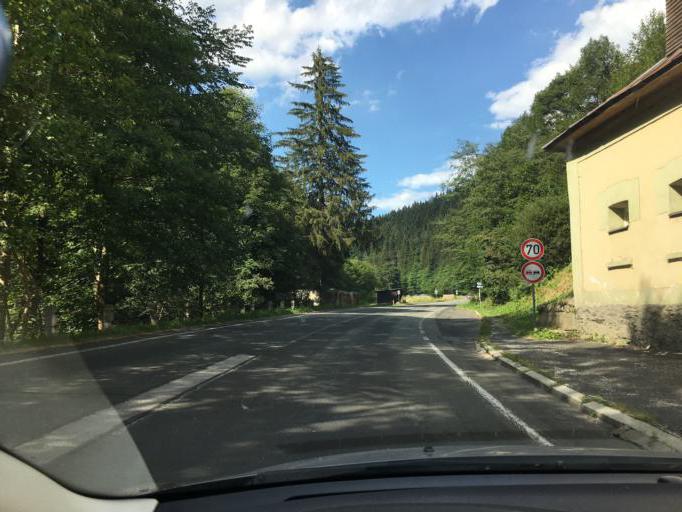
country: CZ
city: Benecko
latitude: 50.6871
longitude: 15.5781
